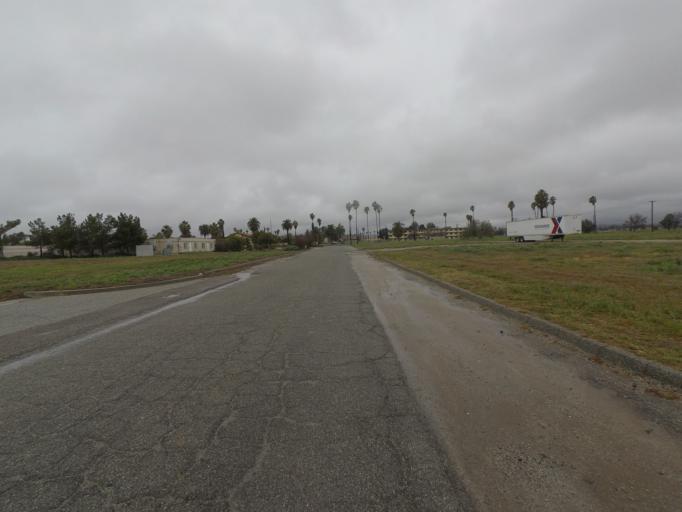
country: US
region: California
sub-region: Riverside County
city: March Air Force Base
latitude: 33.9014
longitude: -117.2509
